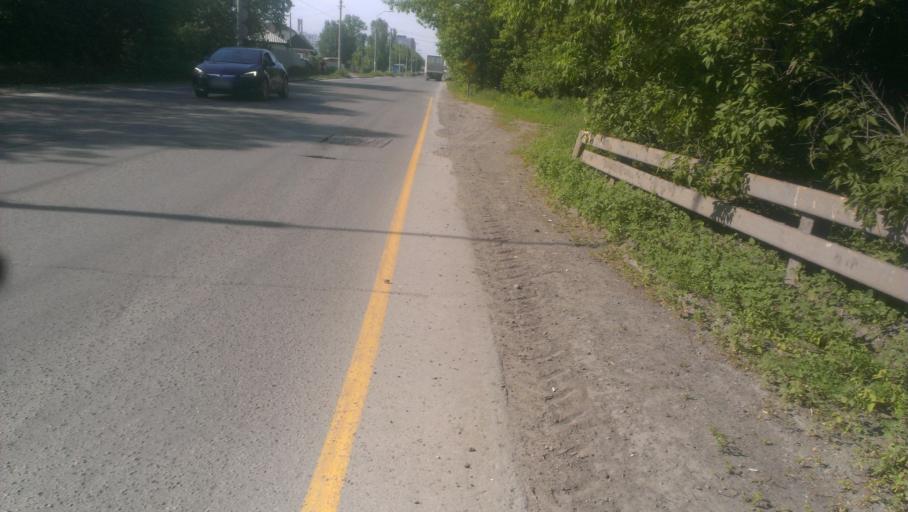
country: RU
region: Altai Krai
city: Novoaltaysk
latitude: 53.4051
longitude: 83.9450
